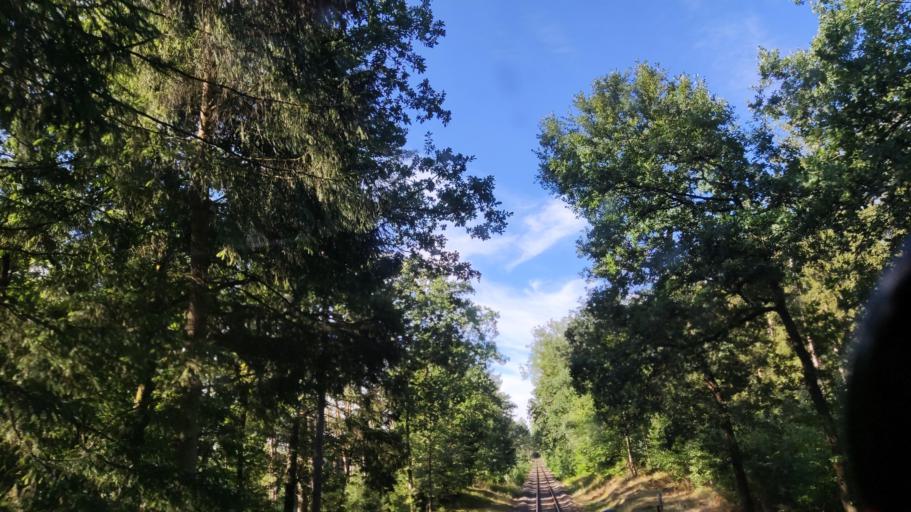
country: DE
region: Lower Saxony
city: Bispingen
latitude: 53.0733
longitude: 9.9876
